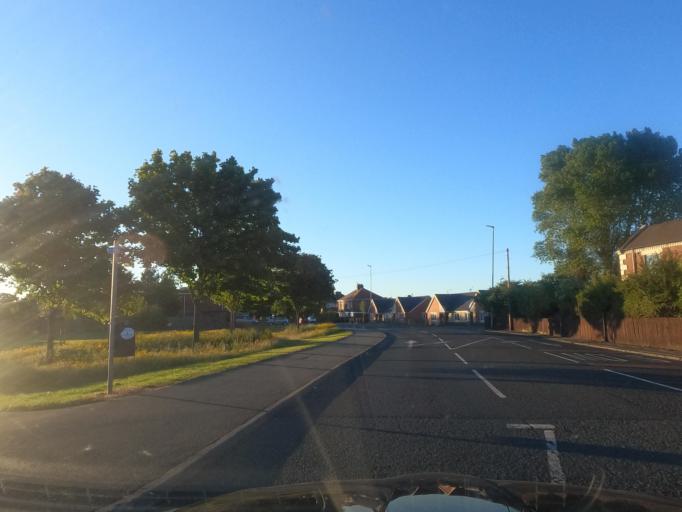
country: GB
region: England
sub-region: Northumberland
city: Blyth
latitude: 55.1287
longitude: -1.5209
